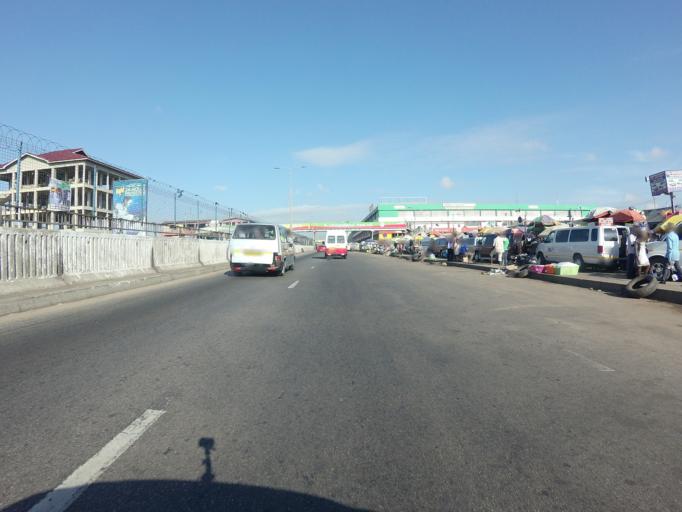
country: GH
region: Greater Accra
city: Accra
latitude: 5.5648
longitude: -0.2351
